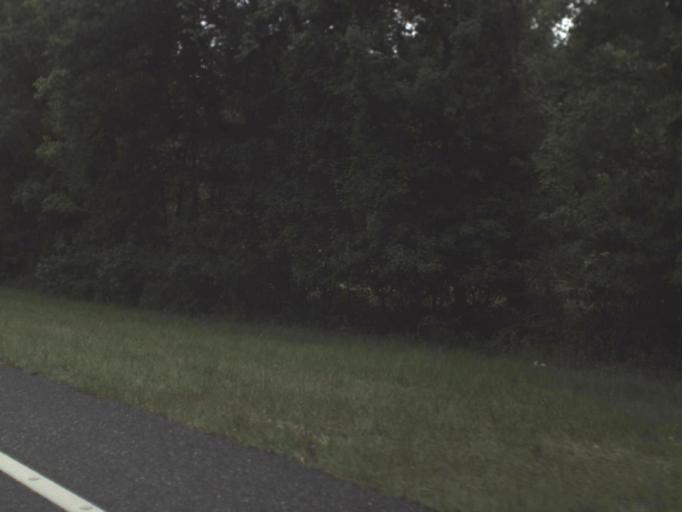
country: US
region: Florida
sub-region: Levy County
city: Williston Highlands
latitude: 29.2593
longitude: -82.7268
